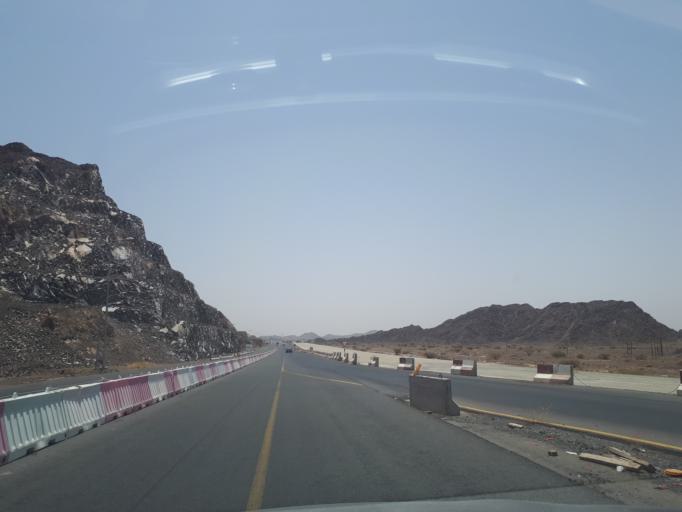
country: OM
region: Ash Sharqiyah
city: Ibra'
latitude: 22.6833
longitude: 58.5831
